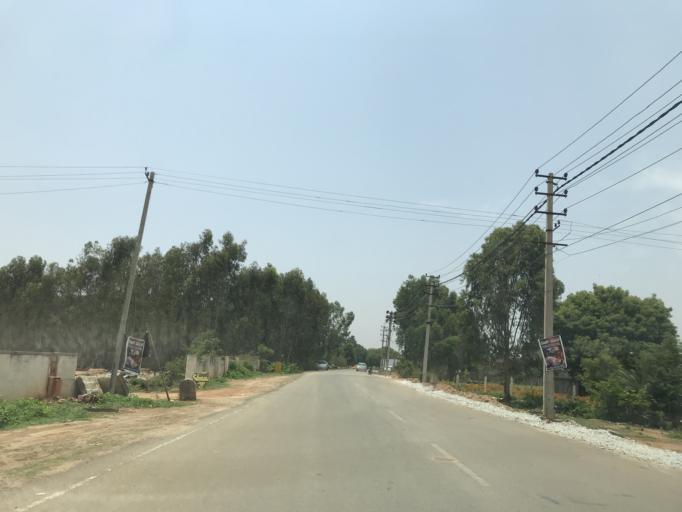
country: IN
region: Karnataka
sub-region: Bangalore Rural
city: Devanhalli
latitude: 13.1812
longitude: 77.6697
